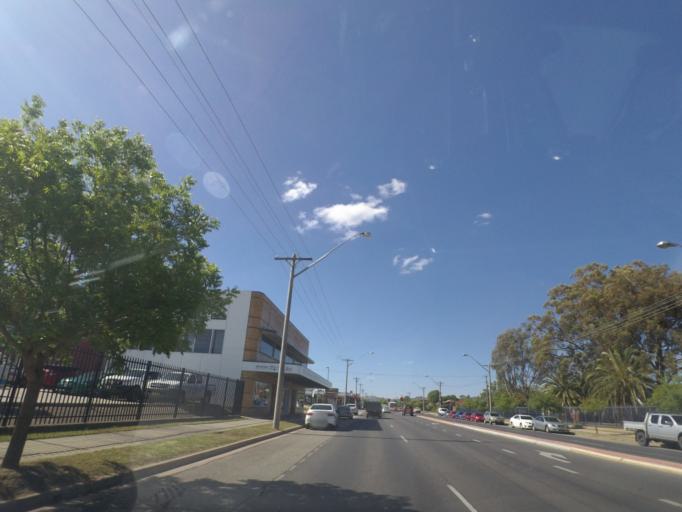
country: AU
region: New South Wales
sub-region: Albury Municipality
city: North Albury
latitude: -36.0640
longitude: 146.9313
